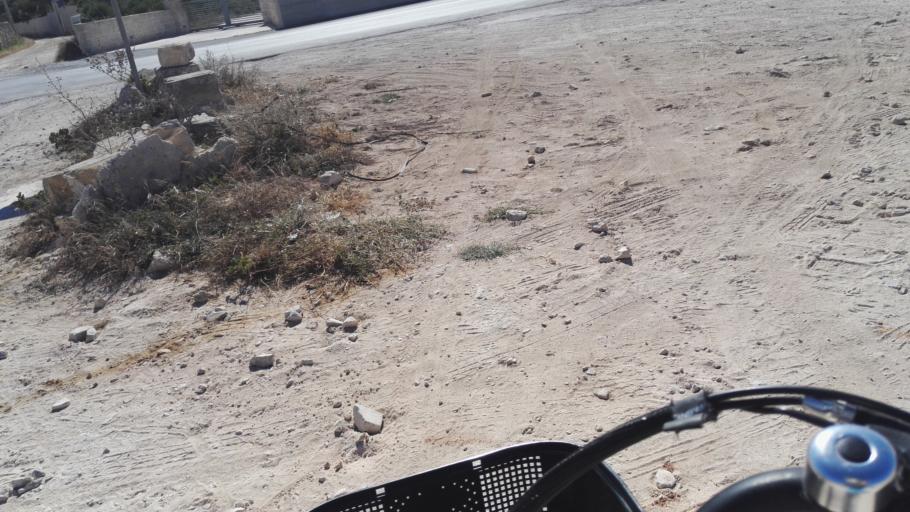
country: IT
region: Sicily
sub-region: Trapani
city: Favignana
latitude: 37.9341
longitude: 12.3340
